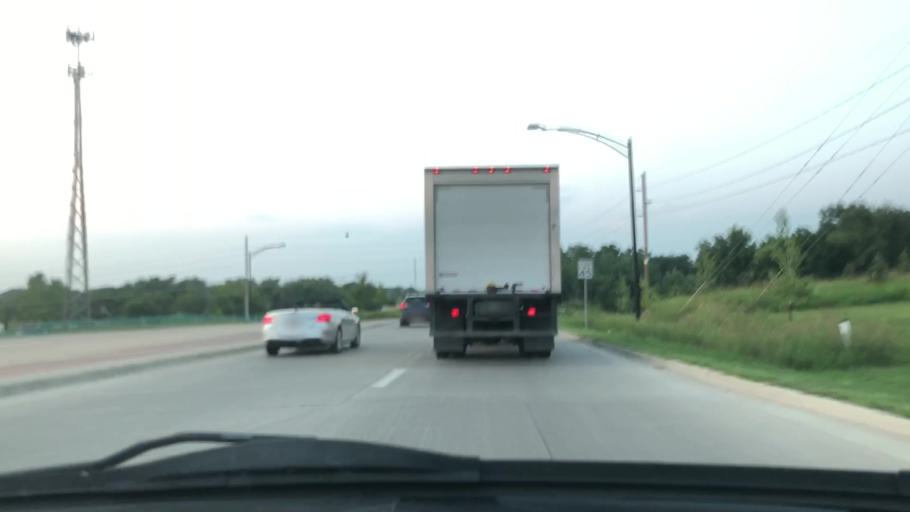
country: US
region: Iowa
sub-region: Johnson County
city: Coralville
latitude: 41.7009
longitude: -91.6082
